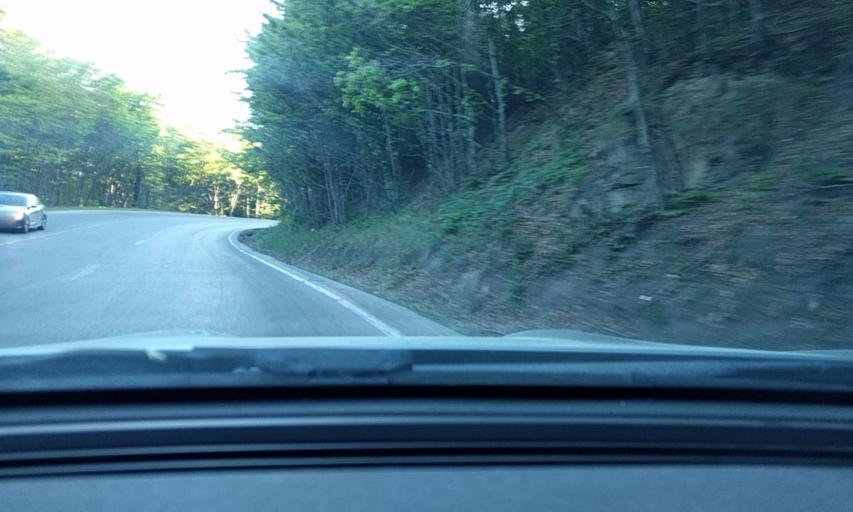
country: RO
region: Covasna
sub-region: Comuna Bretcu
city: Bretcu
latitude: 46.0656
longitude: 26.3706
